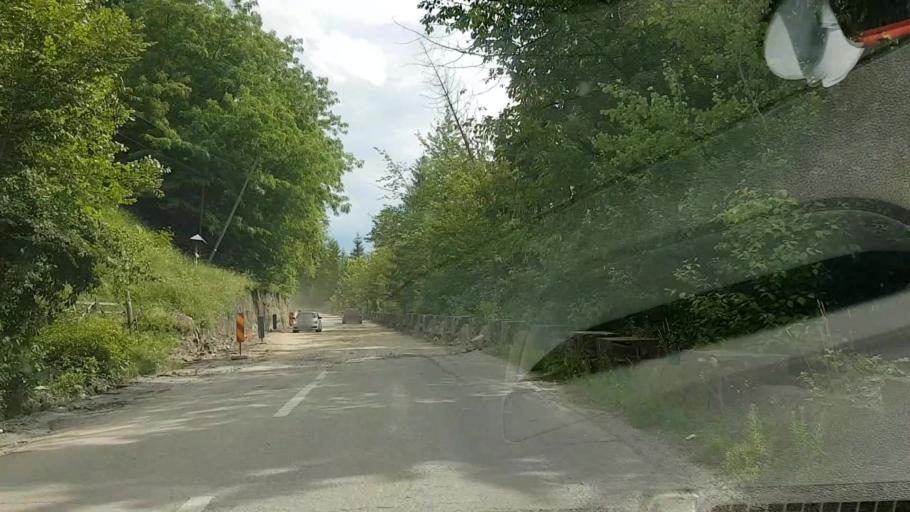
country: RO
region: Neamt
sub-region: Comuna Hangu
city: Hangu
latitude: 47.0534
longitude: 26.0382
